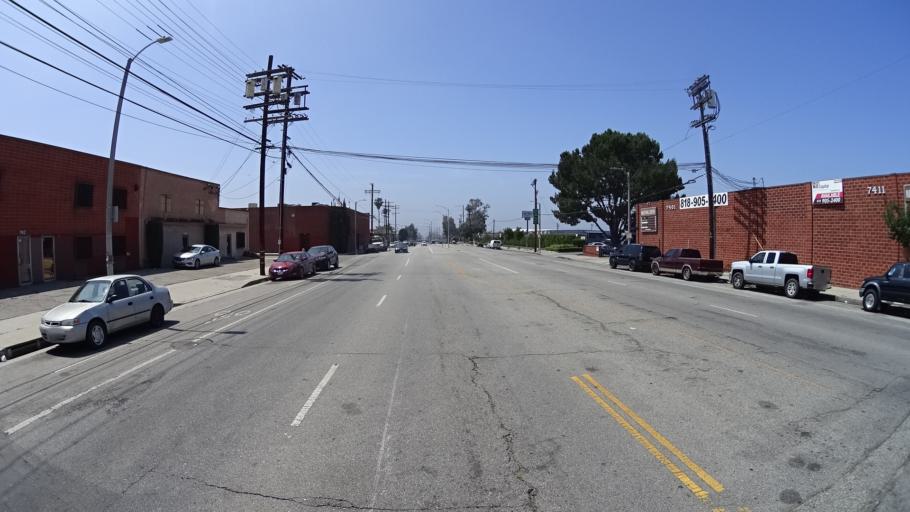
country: US
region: California
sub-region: Los Angeles County
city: North Hollywood
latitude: 34.2053
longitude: -118.3964
